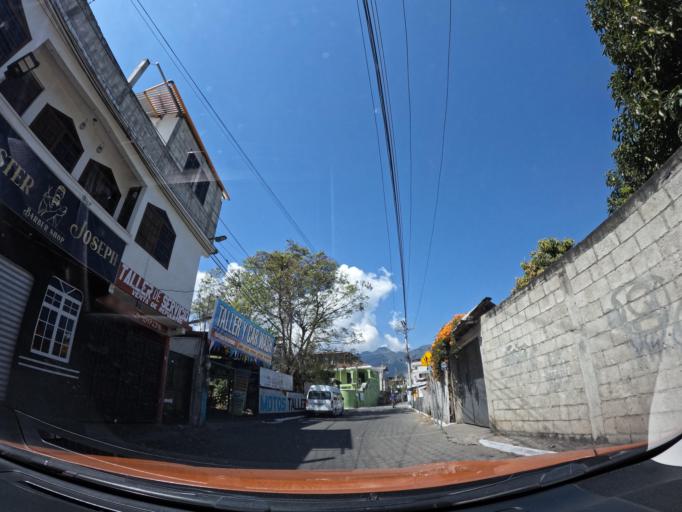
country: GT
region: Solola
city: San Pedro La Laguna
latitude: 14.6911
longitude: -91.2687
